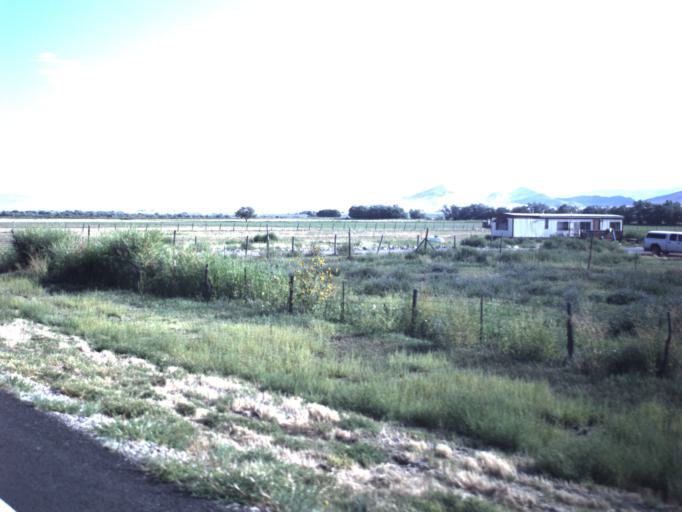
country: US
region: Utah
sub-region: Sevier County
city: Salina
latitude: 38.9766
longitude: -111.8604
